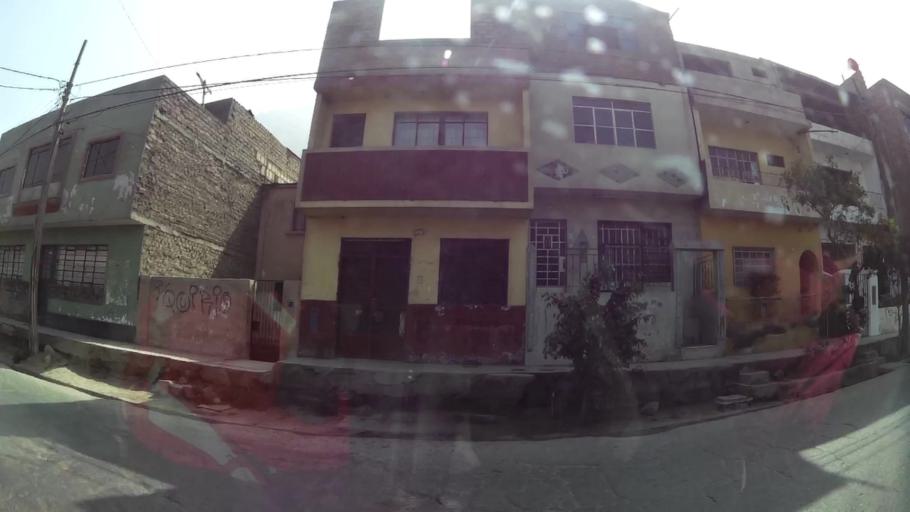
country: PE
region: Lima
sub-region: Lima
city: Asentamiento Humano Nicolas de Pierola
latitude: -11.9260
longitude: -76.6861
